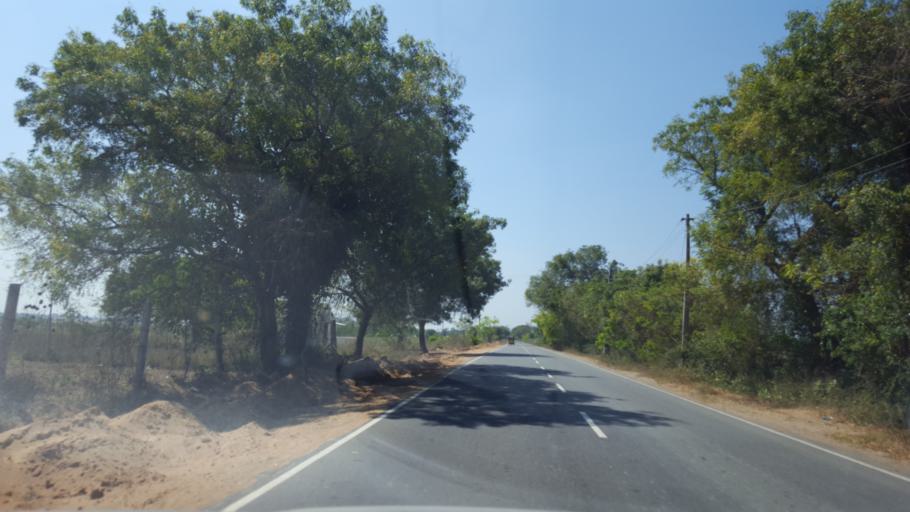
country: IN
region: Tamil Nadu
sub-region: Kancheepuram
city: Wallajahbad
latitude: 12.7721
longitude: 79.8918
